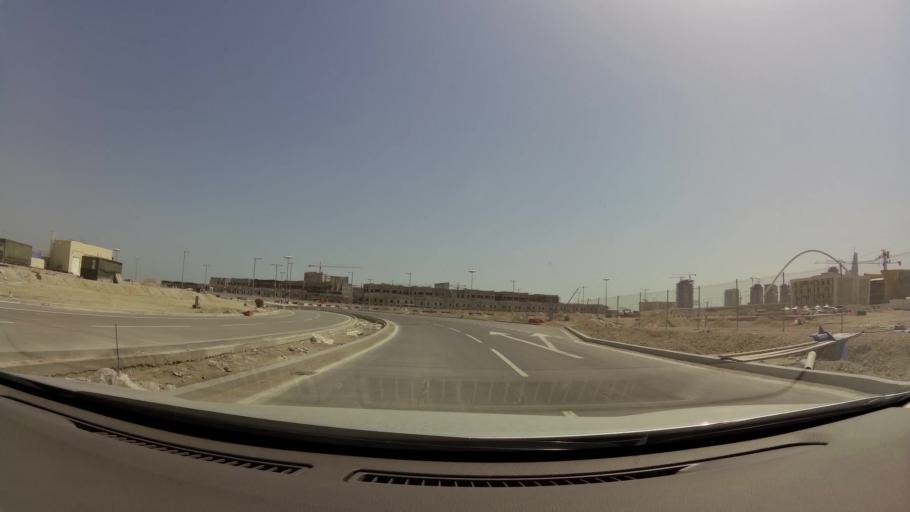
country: QA
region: Baladiyat Umm Salal
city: Umm Salal Muhammad
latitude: 25.4047
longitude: 51.5111
